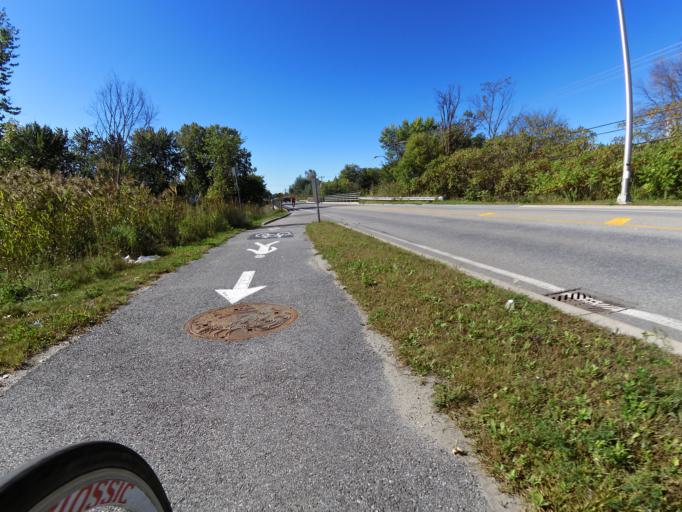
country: CA
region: Quebec
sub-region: Outaouais
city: Gatineau
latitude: 45.5035
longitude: -75.5628
